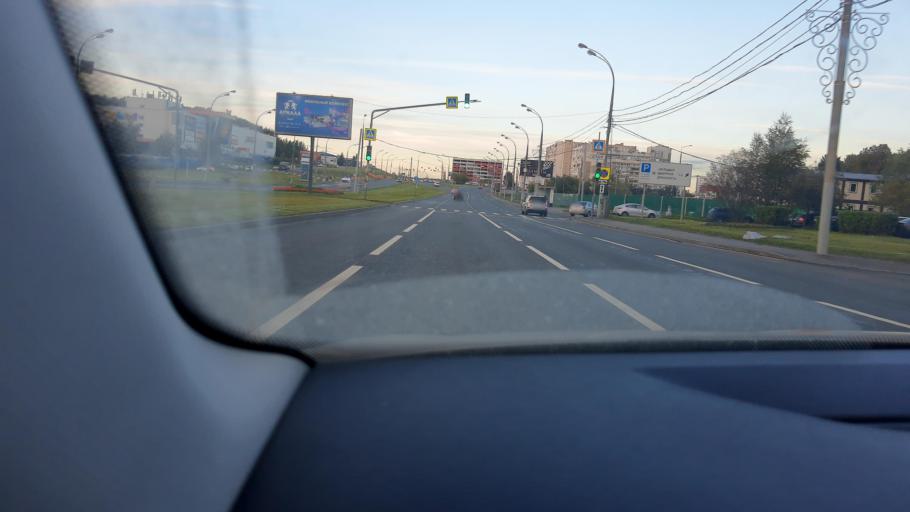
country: RU
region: Moscow
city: Chertanovo Yuzhnoye
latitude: 55.5624
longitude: 37.5579
